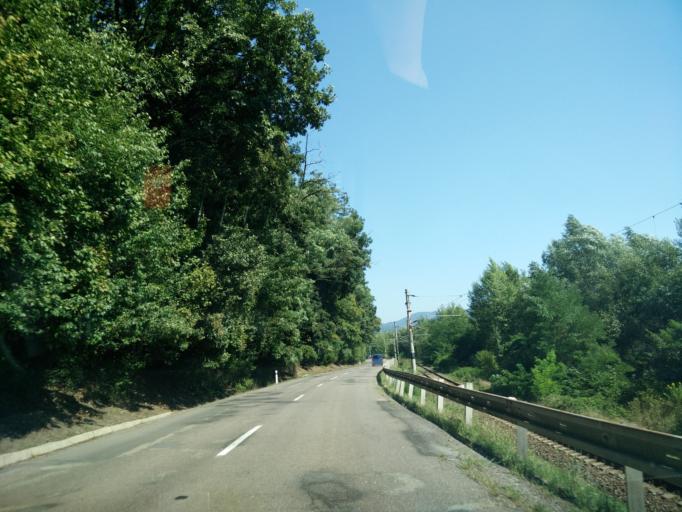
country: SK
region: Banskobystricky
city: Nova Bana
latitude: 48.3683
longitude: 18.5863
